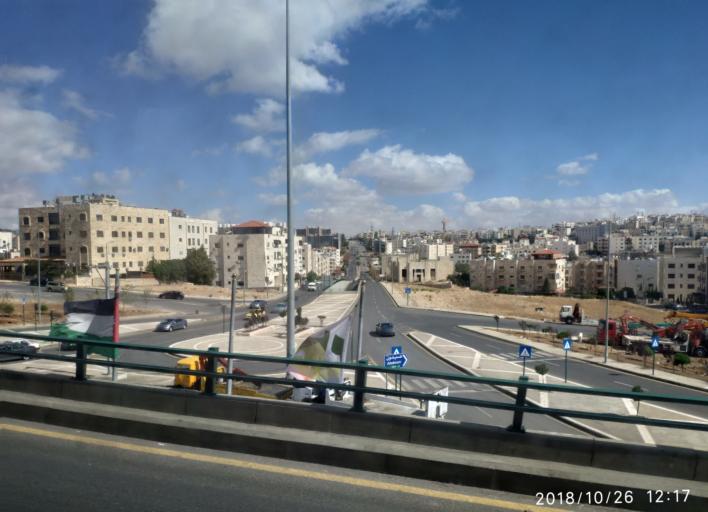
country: JO
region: Amman
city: Wadi as Sir
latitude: 31.9434
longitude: 35.8507
